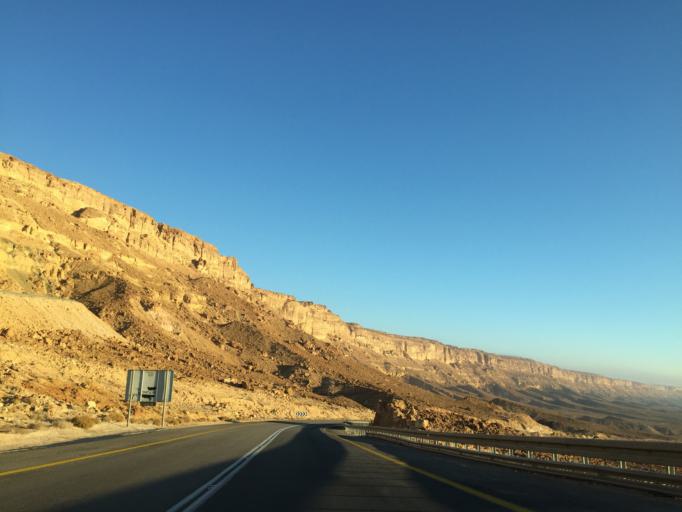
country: IL
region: Southern District
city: Mitzpe Ramon
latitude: 30.6207
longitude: 34.8192
